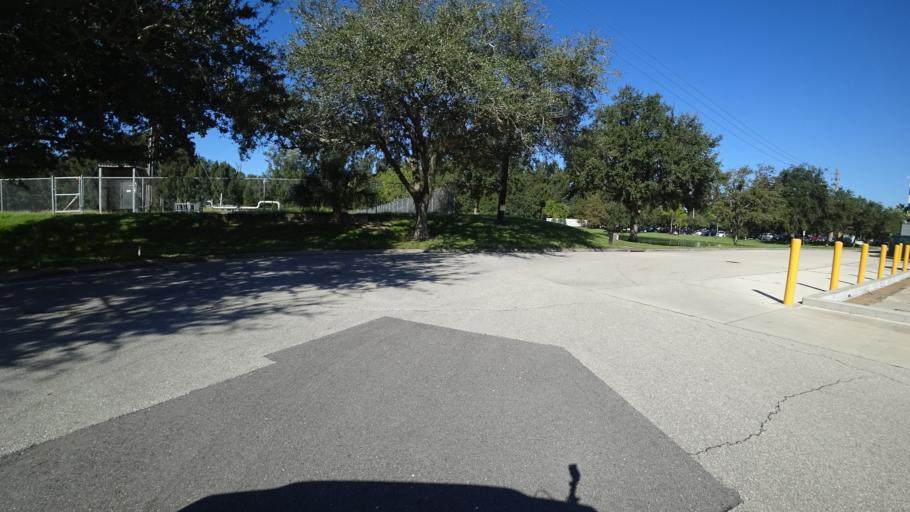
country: US
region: Florida
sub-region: Manatee County
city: West Samoset
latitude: 27.4847
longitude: -82.5568
